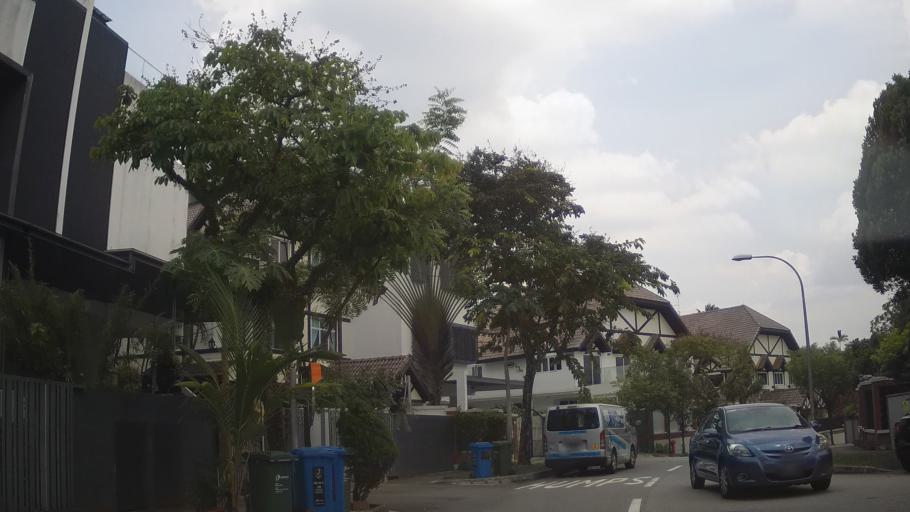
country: MY
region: Johor
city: Johor Bahru
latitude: 1.3715
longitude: 103.7695
